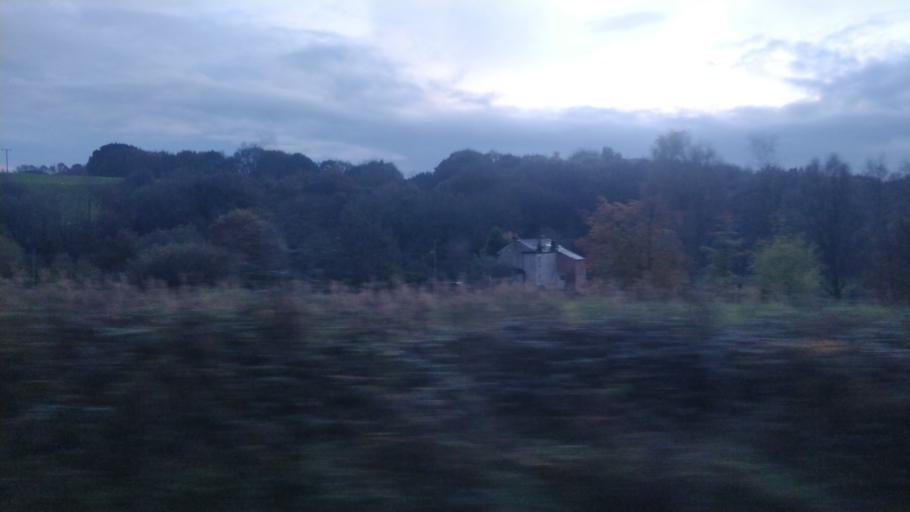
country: GB
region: England
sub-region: Borough of Wigan
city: Shevington
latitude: 53.5621
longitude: -2.7020
